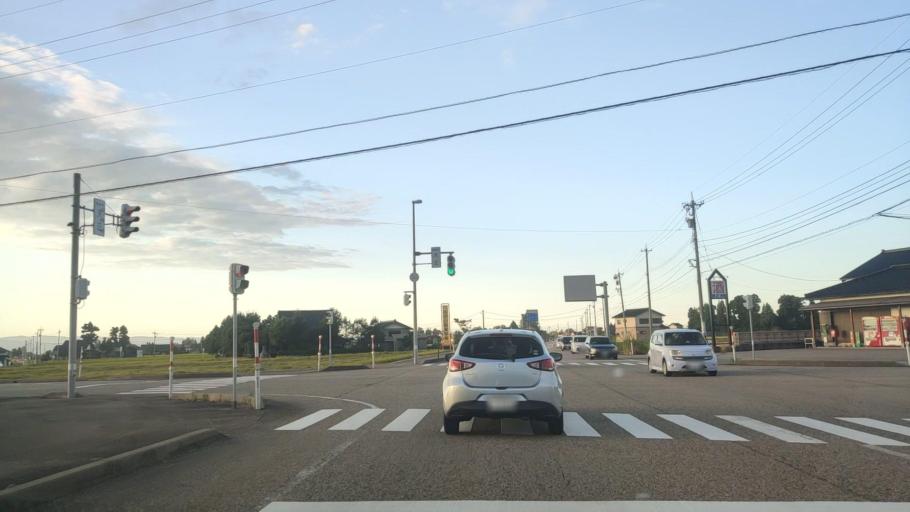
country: JP
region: Toyama
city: Nanto-shi
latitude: 36.5933
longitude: 136.9643
